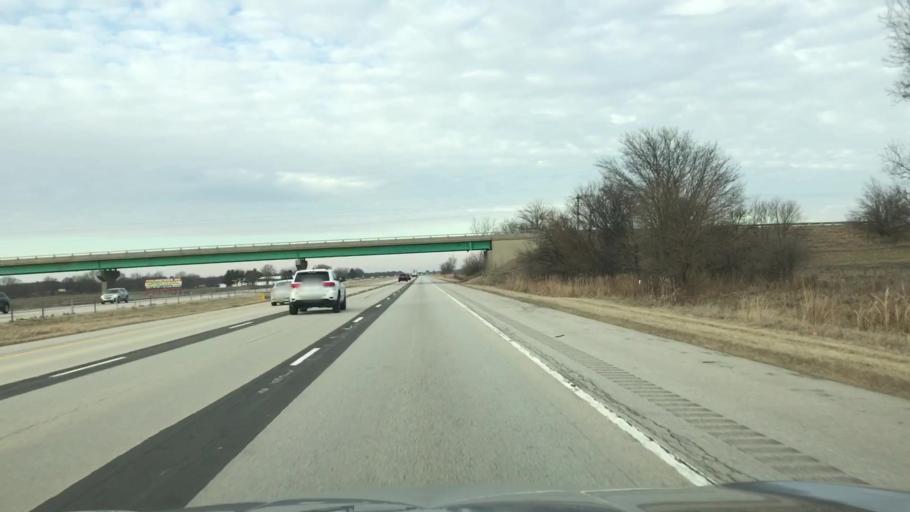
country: US
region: Illinois
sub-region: Sangamon County
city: Chatham
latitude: 39.6469
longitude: -89.6471
